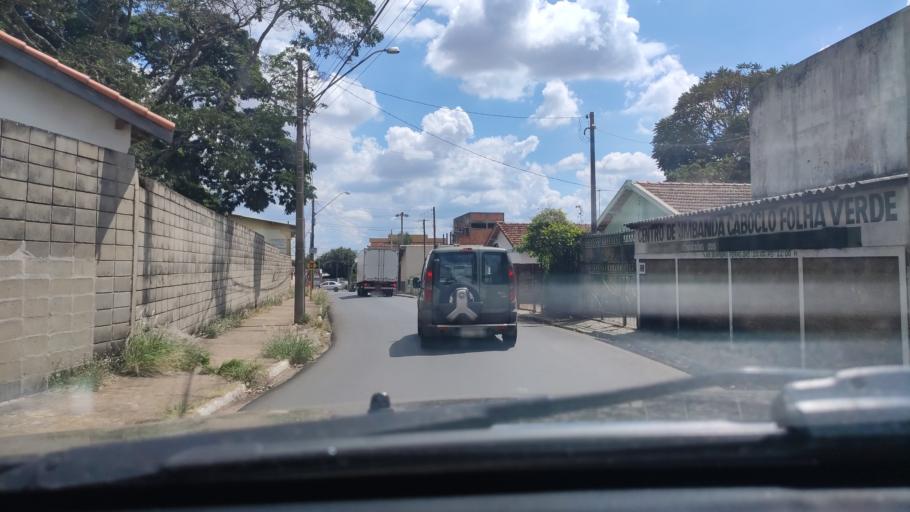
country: BR
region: Sao Paulo
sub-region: Sao Carlos
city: Sao Carlos
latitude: -22.0097
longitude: -47.8693
